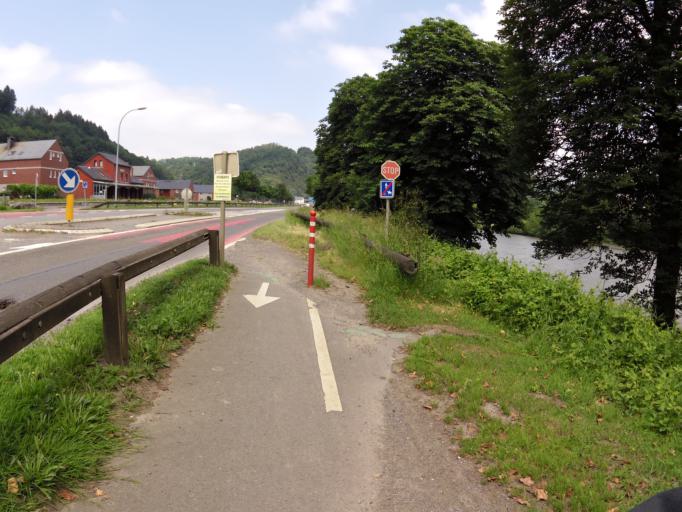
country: BE
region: Wallonia
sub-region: Province de Namur
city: Hastiere-Lavaux
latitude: 50.2117
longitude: 4.8222
